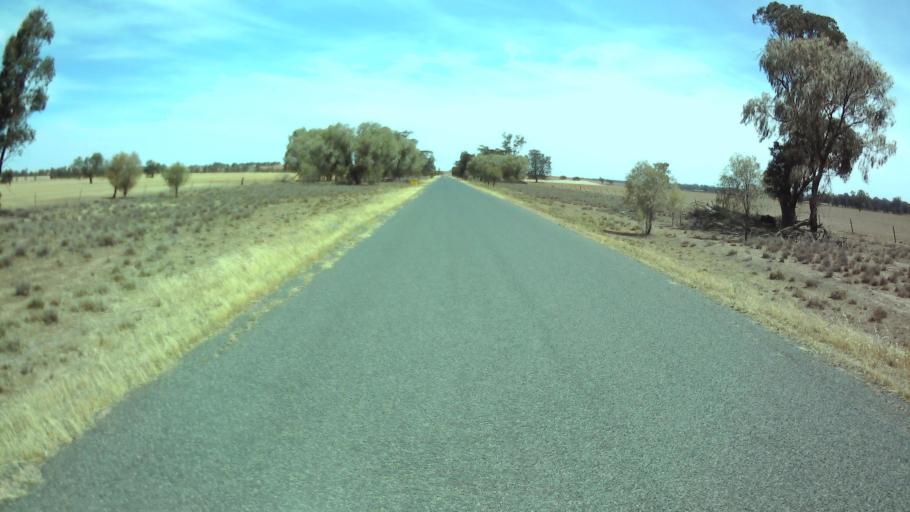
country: AU
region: New South Wales
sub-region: Weddin
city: Grenfell
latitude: -33.8785
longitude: 147.7433
